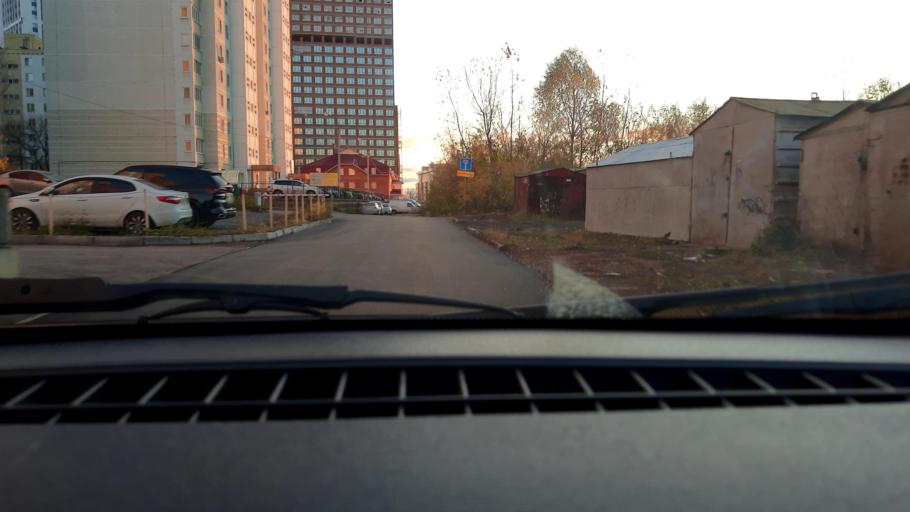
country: RU
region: Bashkortostan
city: Ufa
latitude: 54.7138
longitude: 55.9710
